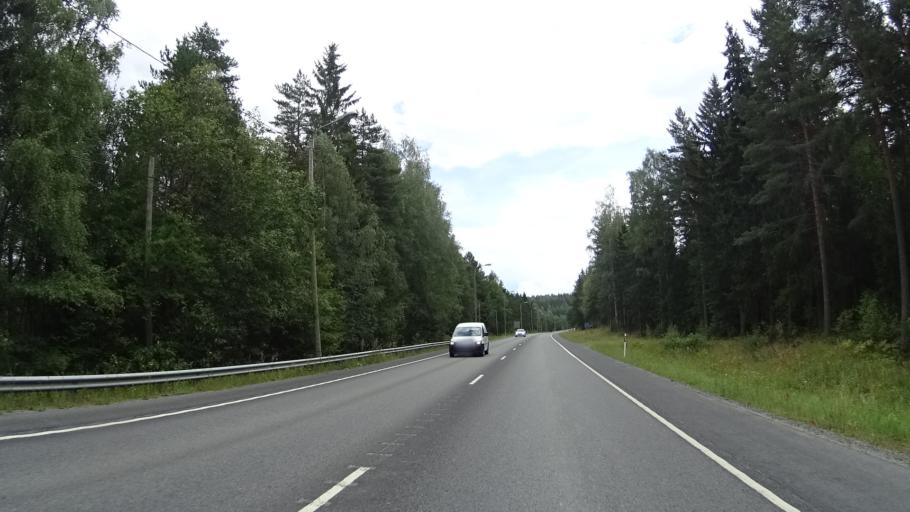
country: FI
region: Pirkanmaa
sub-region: Tampere
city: Kangasala
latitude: 61.4449
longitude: 24.1121
